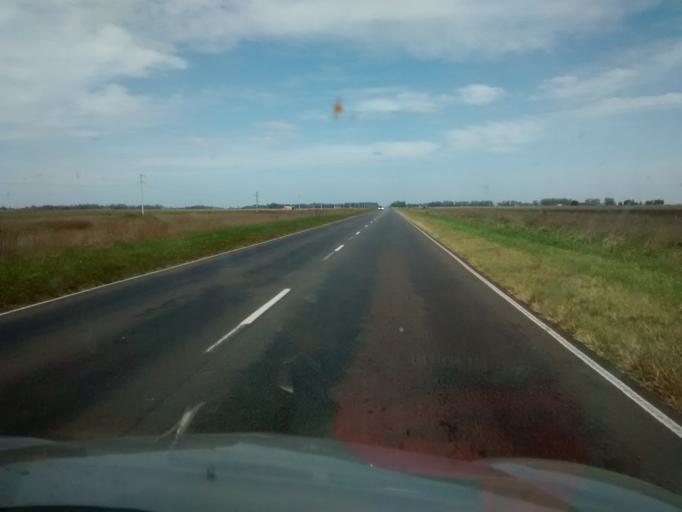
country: AR
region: Buenos Aires
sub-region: Partido de Ayacucho
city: Ayacucho
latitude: -37.0957
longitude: -58.5474
